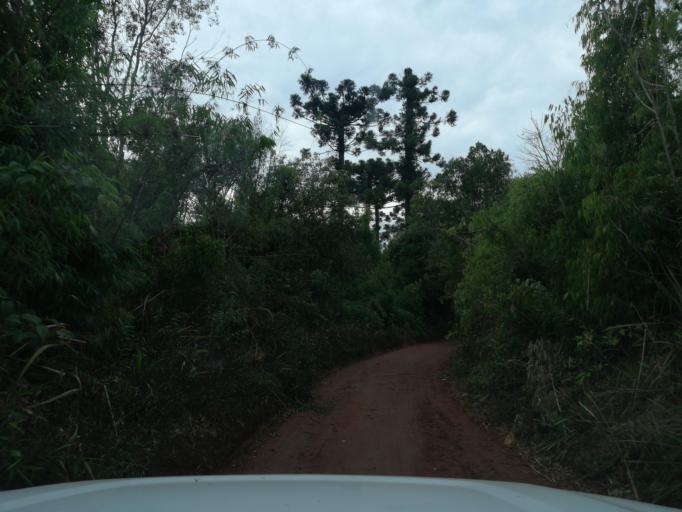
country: AR
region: Misiones
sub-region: Departamento de San Pedro
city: San Pedro
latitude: -26.6313
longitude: -54.0978
